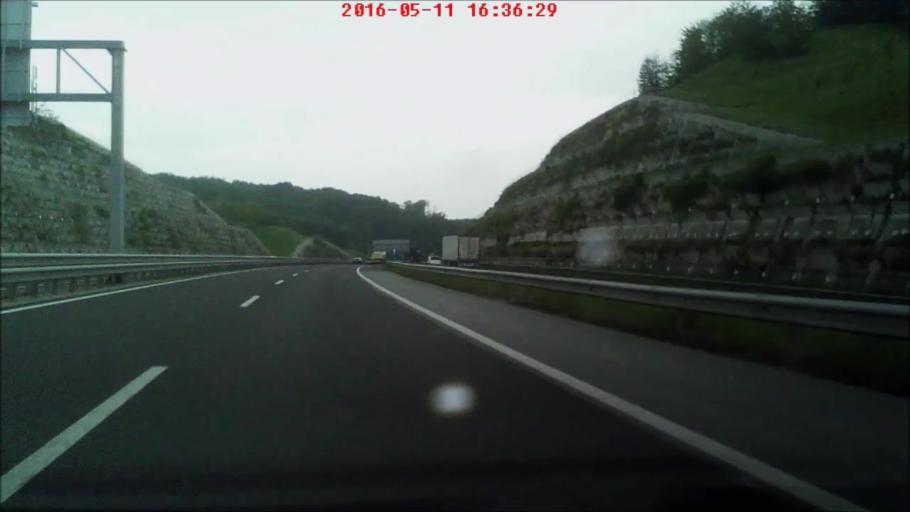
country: SI
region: Pesnica
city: Pesnica pri Mariboru
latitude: 46.5847
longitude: 15.6882
